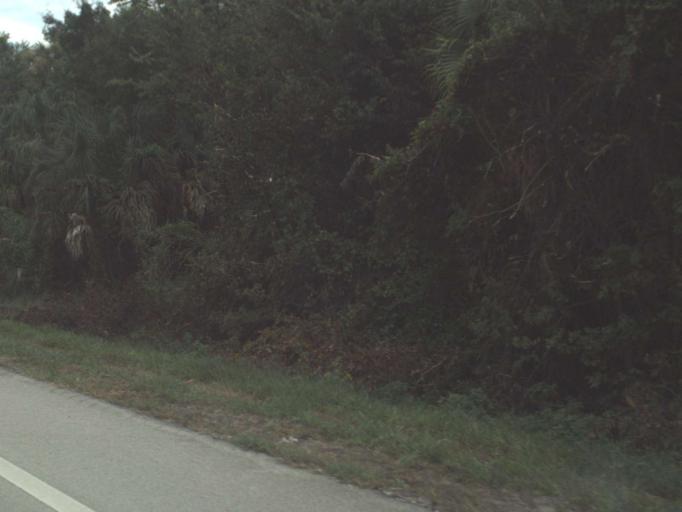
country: US
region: Florida
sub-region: Martin County
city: Indiantown
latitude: 27.0127
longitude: -80.6268
